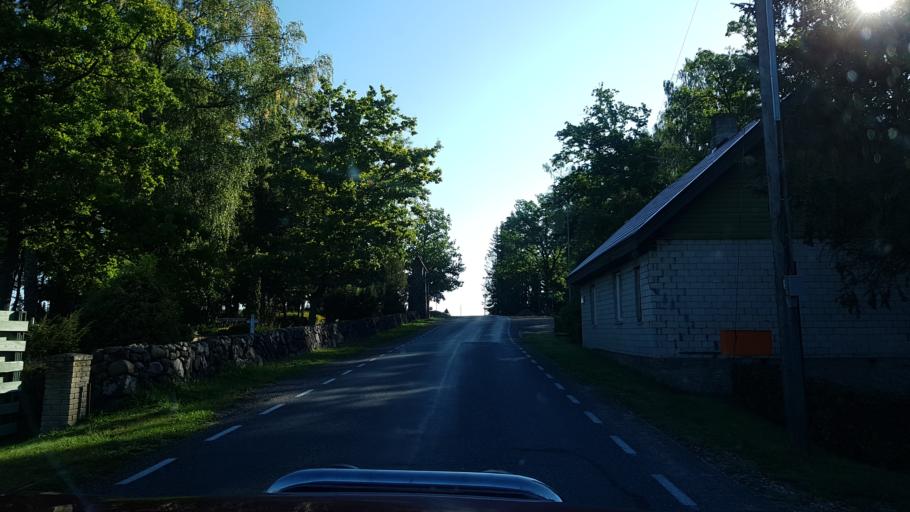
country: EE
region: Jogevamaa
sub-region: Tabivere vald
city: Tabivere
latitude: 58.6839
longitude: 26.5924
